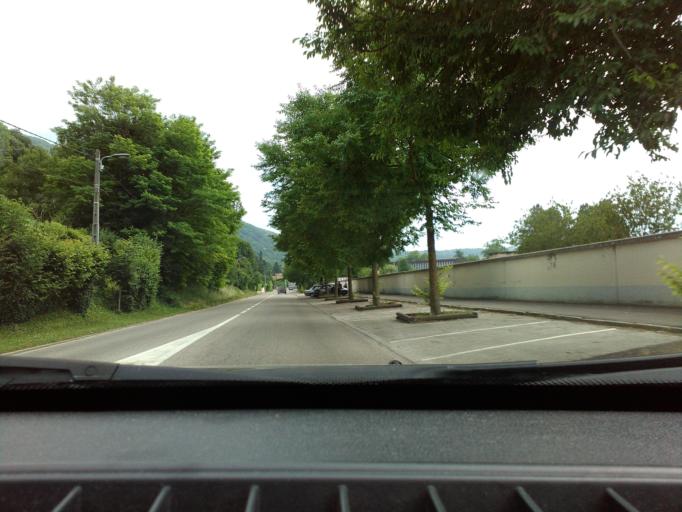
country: FR
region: Rhone-Alpes
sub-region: Departement de l'Isere
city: Saint-Martin-d'Heres
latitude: 45.1716
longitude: 5.7686
